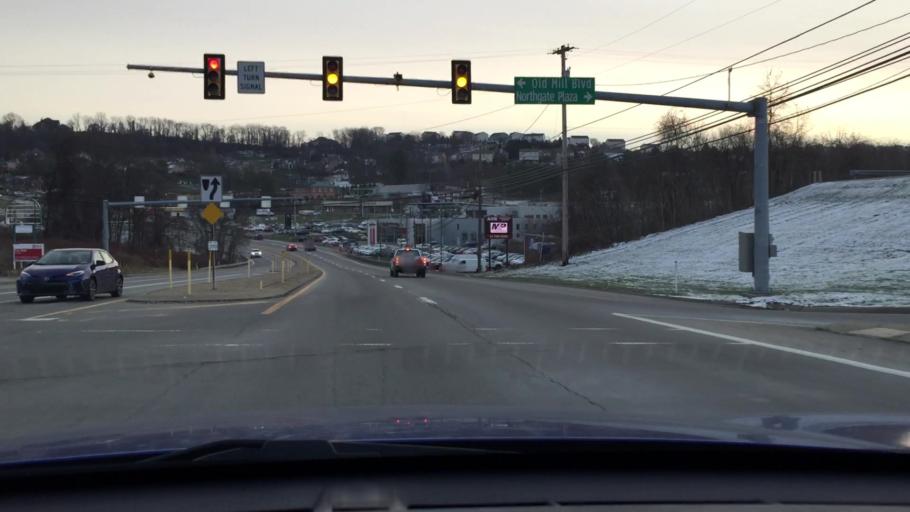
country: US
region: Pennsylvania
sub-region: Washington County
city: East Washington
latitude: 40.1884
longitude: -80.2163
